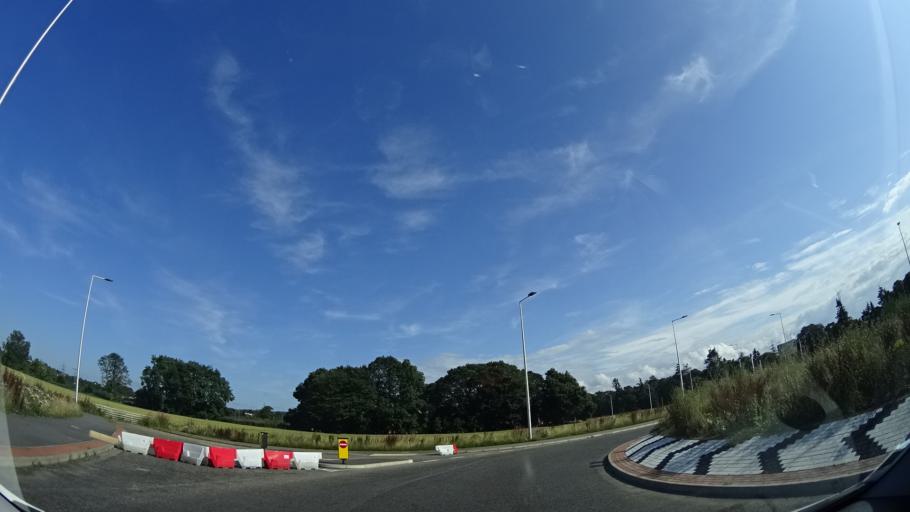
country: GB
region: Scotland
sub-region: Highland
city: Inverness
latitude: 57.4528
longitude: -4.2566
